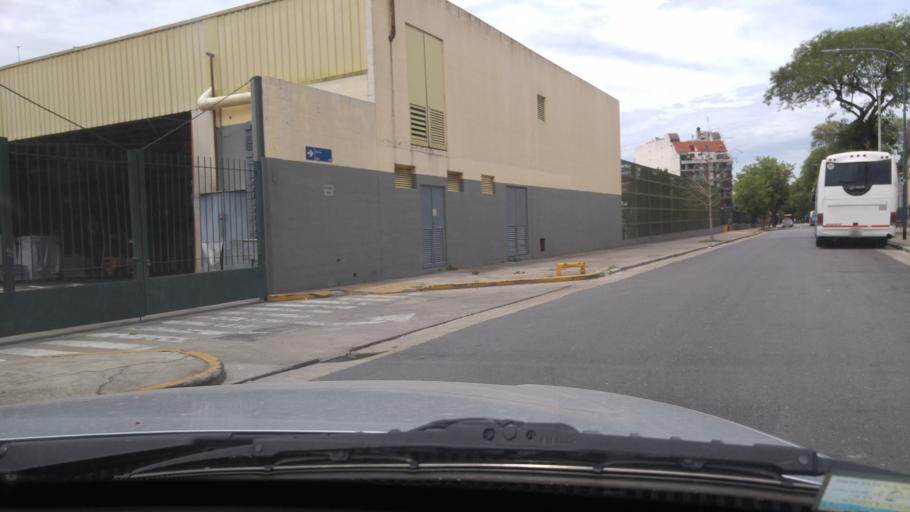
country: AR
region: Buenos Aires F.D.
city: Villa Santa Rita
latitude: -34.6309
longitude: -58.5210
